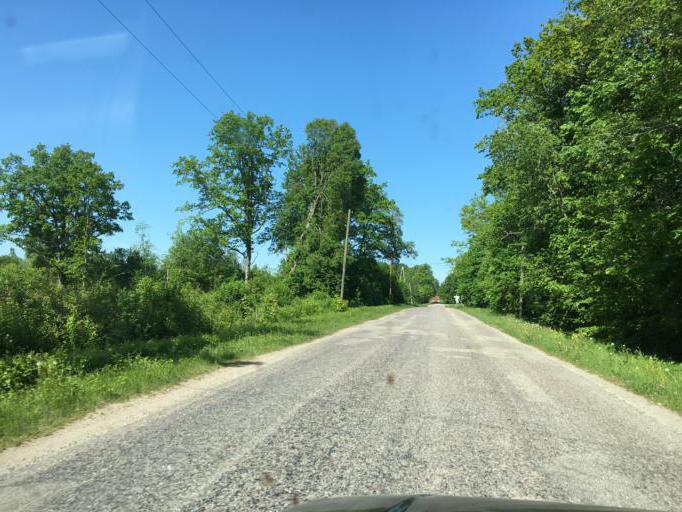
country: LV
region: Dundaga
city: Dundaga
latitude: 57.4978
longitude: 22.3484
